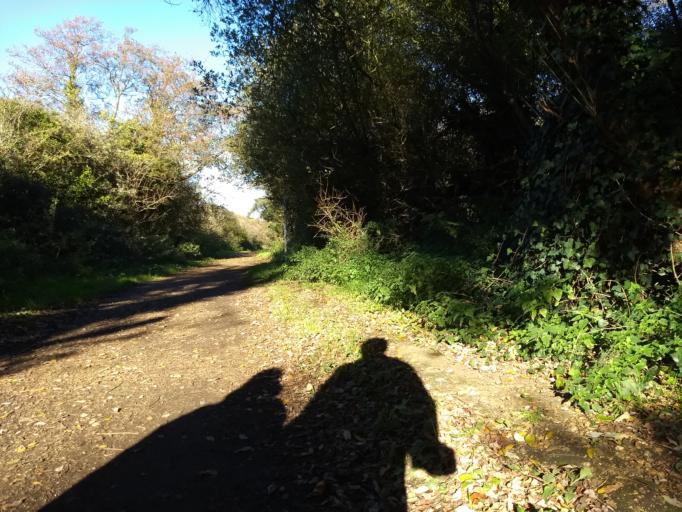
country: GB
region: England
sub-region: Isle of Wight
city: Newport
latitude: 50.6851
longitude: -1.2905
